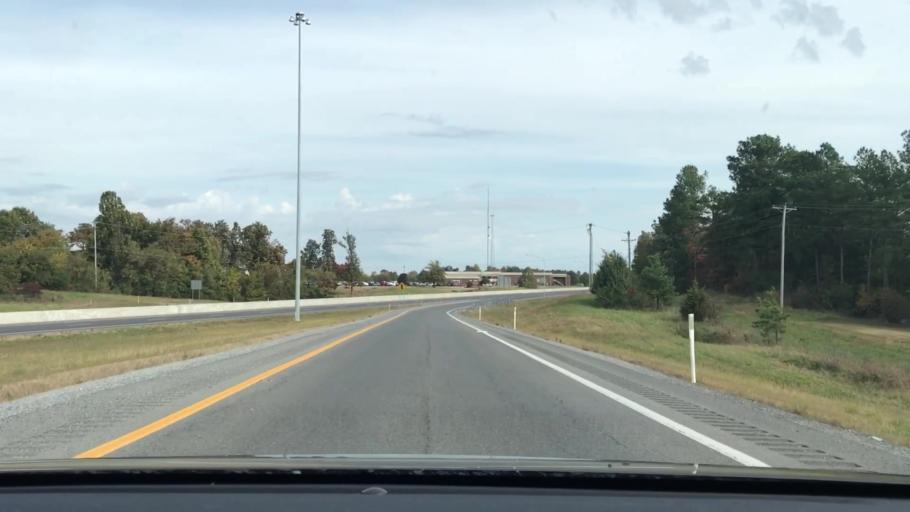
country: US
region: Kentucky
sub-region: Graves County
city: Mayfield
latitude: 36.7576
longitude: -88.6547
